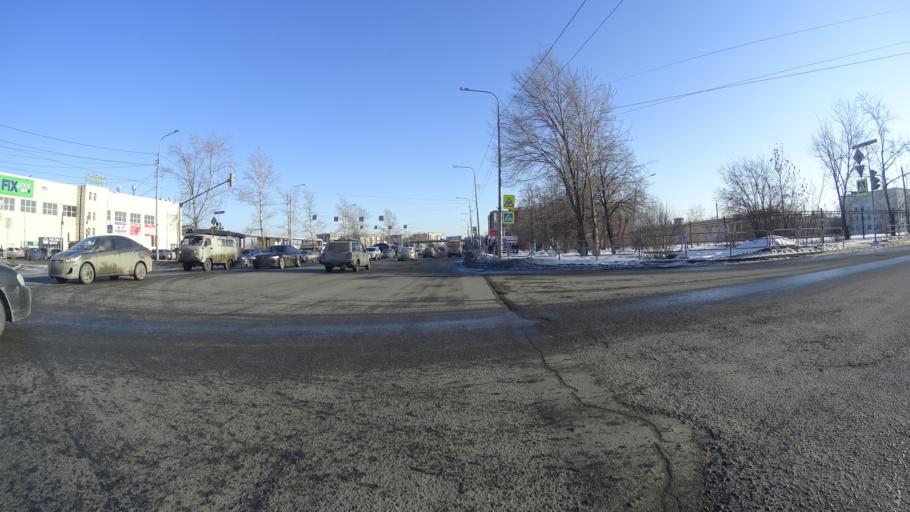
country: RU
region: Chelyabinsk
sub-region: Gorod Chelyabinsk
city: Chelyabinsk
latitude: 55.2037
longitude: 61.3242
